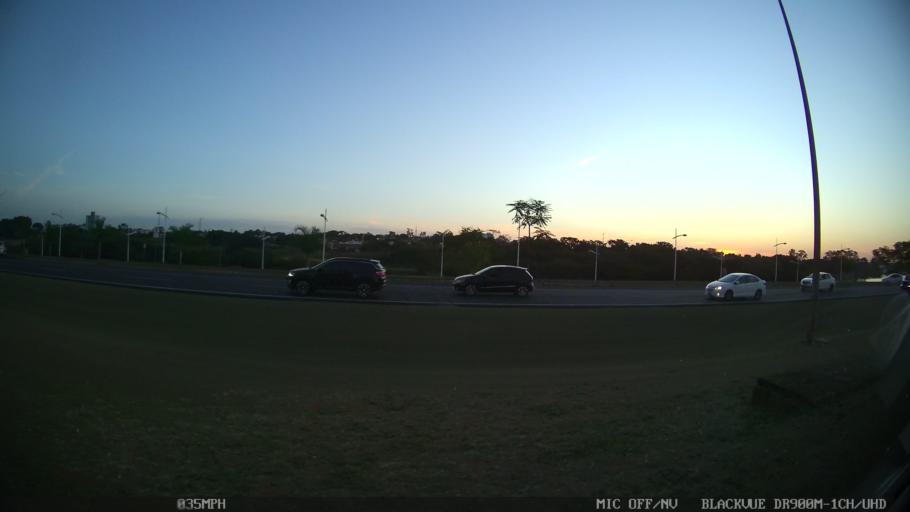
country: BR
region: Sao Paulo
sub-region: Sao Jose Do Rio Preto
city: Sao Jose do Rio Preto
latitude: -20.8178
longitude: -49.3467
